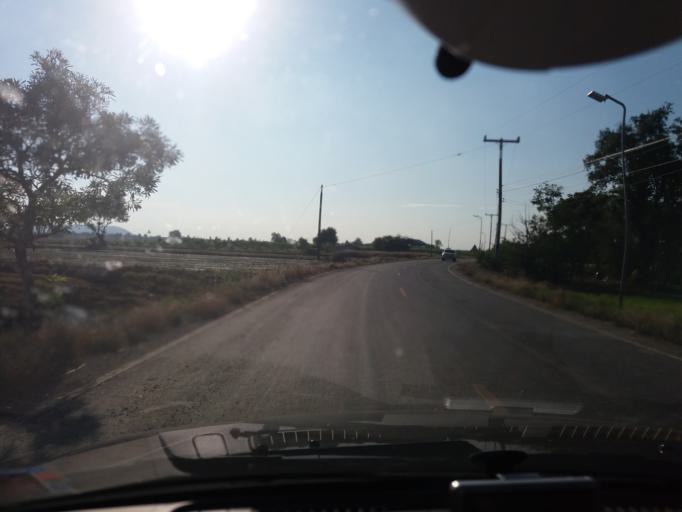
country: TH
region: Suphan Buri
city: Doem Bang Nang Buat
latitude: 14.9128
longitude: 100.1451
